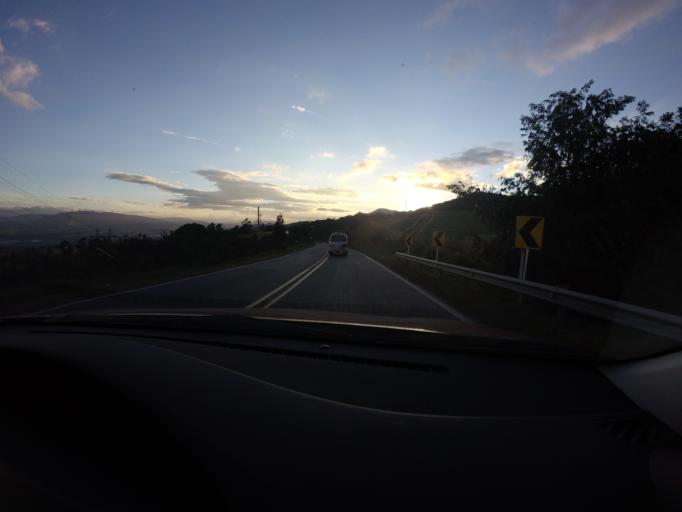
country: CO
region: Cundinamarca
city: Sutatausa
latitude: 5.1661
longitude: -73.8909
